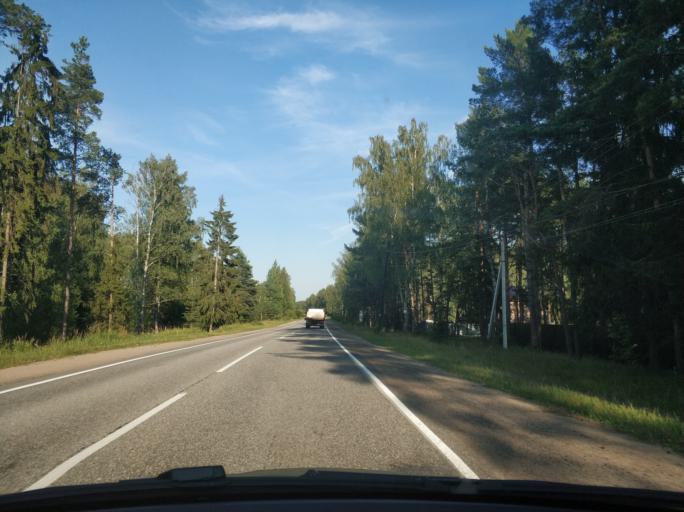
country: RU
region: Leningrad
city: Borisova Griva
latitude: 60.0925
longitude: 30.9885
